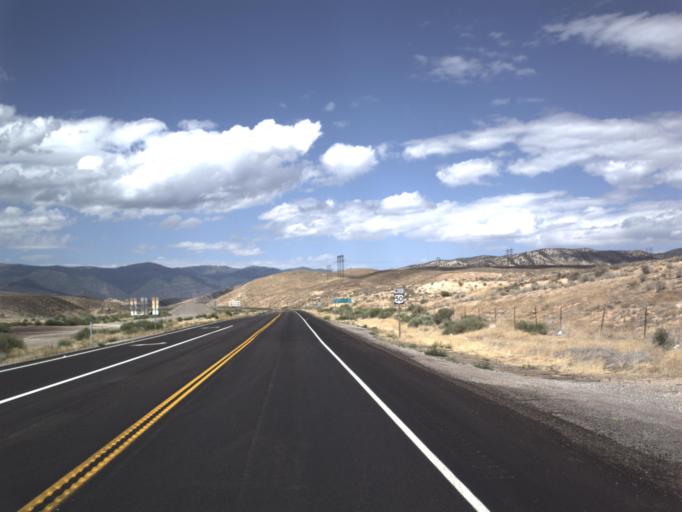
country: US
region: Utah
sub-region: Sevier County
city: Aurora
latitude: 38.9589
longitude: -111.9249
